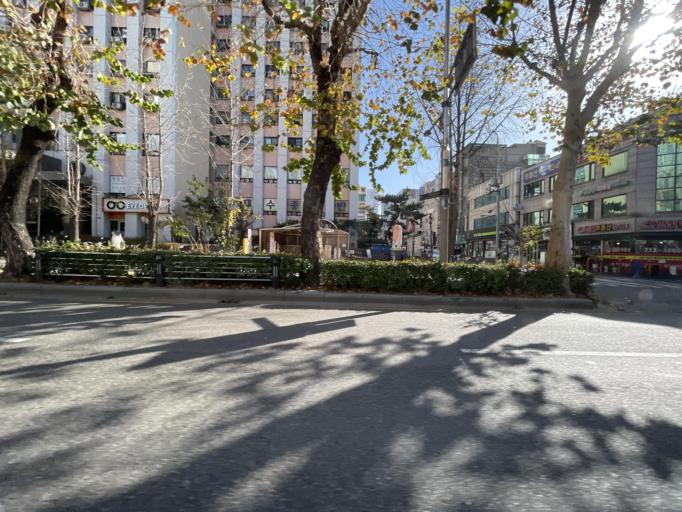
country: KR
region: Seoul
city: Seoul
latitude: 37.5512
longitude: 126.9557
